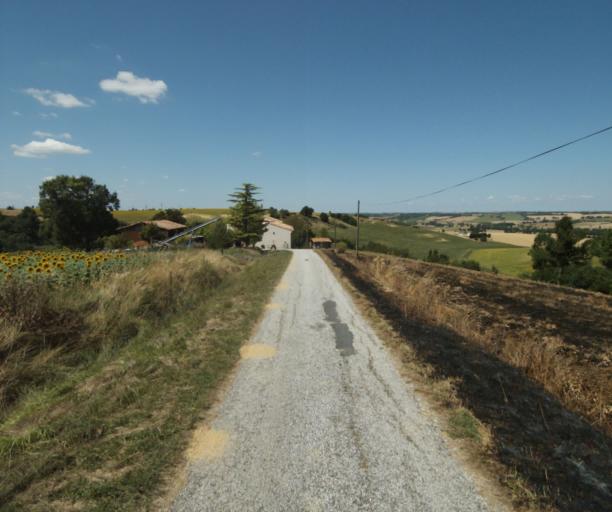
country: FR
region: Midi-Pyrenees
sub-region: Departement de la Haute-Garonne
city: Saint-Felix-Lauragais
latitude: 43.4646
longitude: 1.8784
